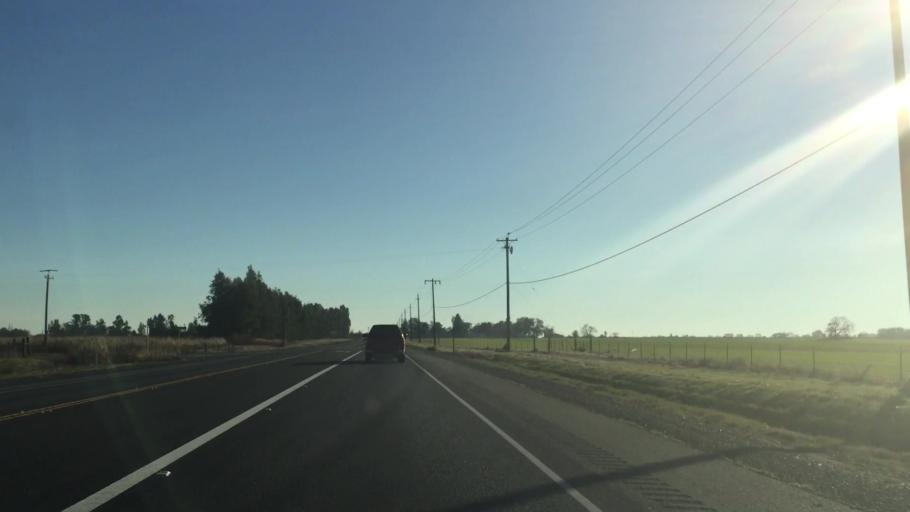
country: US
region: California
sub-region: Butte County
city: Palermo
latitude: 39.4161
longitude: -121.6051
